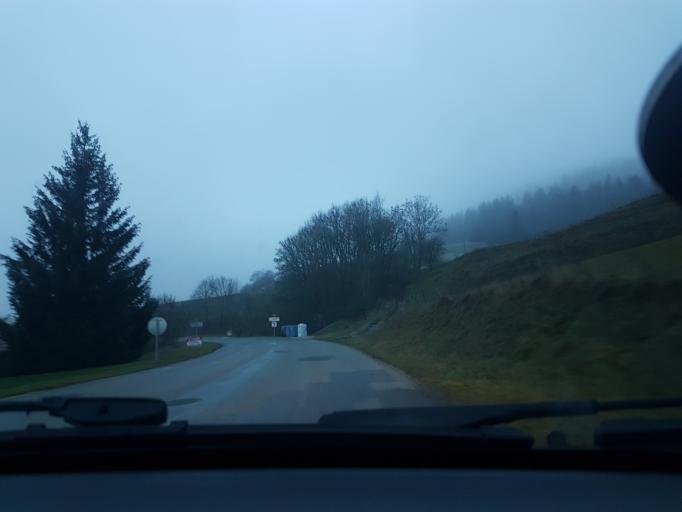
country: FR
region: Franche-Comte
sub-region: Departement du Doubs
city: La Cluse-et-Mijoux
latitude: 46.8963
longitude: 6.4468
